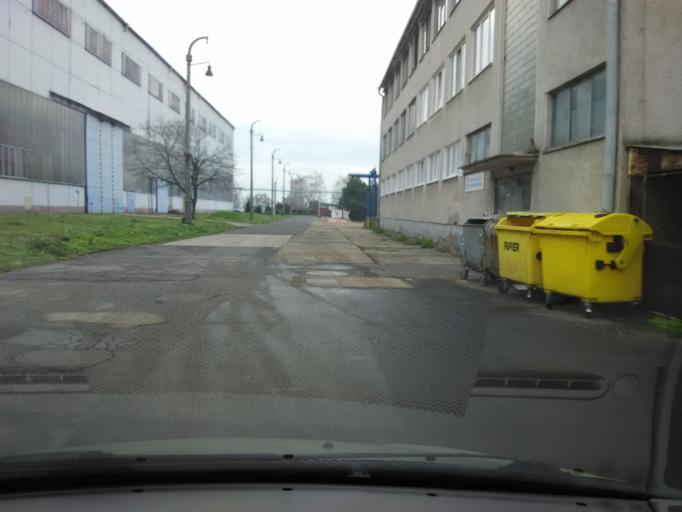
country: SK
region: Nitriansky
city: Tlmace
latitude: 48.2927
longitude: 18.5402
